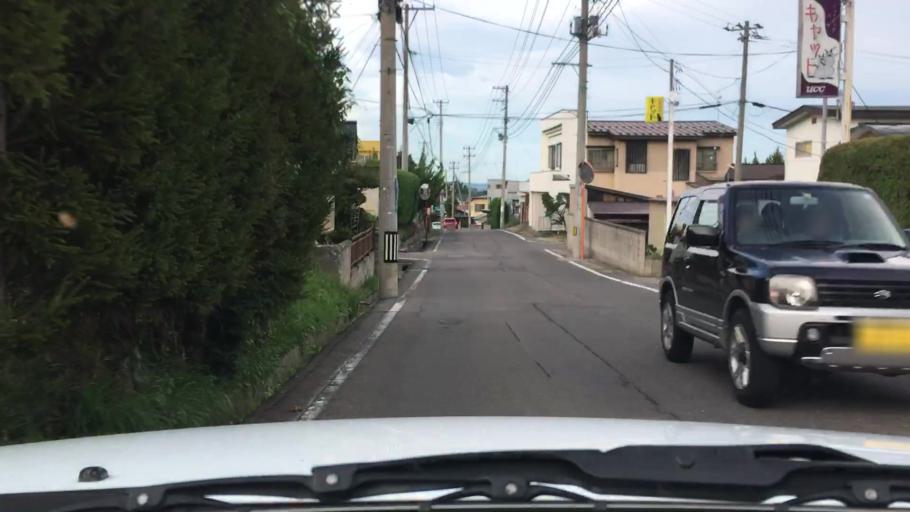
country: JP
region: Aomori
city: Hirosaki
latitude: 40.5809
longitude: 140.4582
